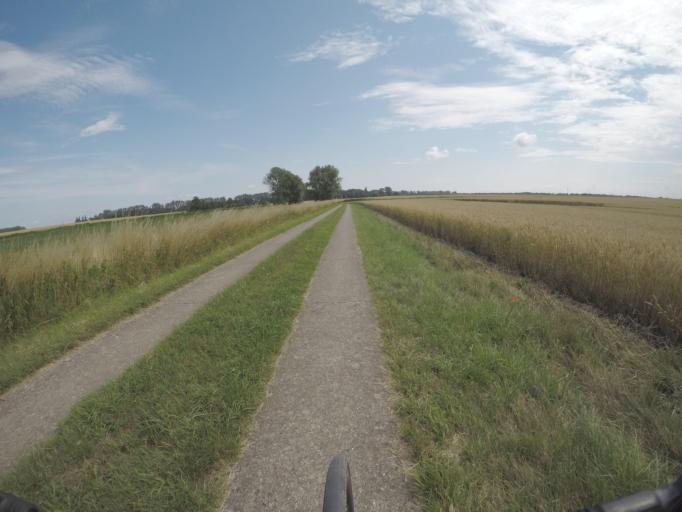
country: DE
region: Mecklenburg-Vorpommern
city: Altefahr
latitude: 54.3690
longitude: 13.1384
